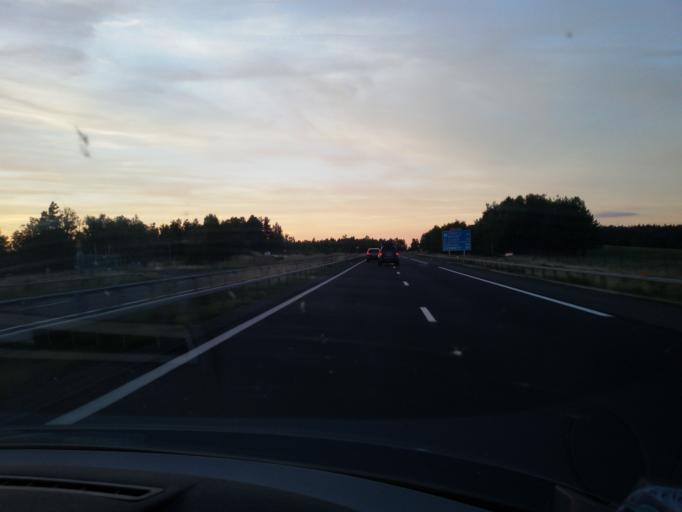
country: FR
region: Languedoc-Roussillon
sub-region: Departement de la Lozere
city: Le Malzieu-Ville
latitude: 44.8308
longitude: 3.2615
